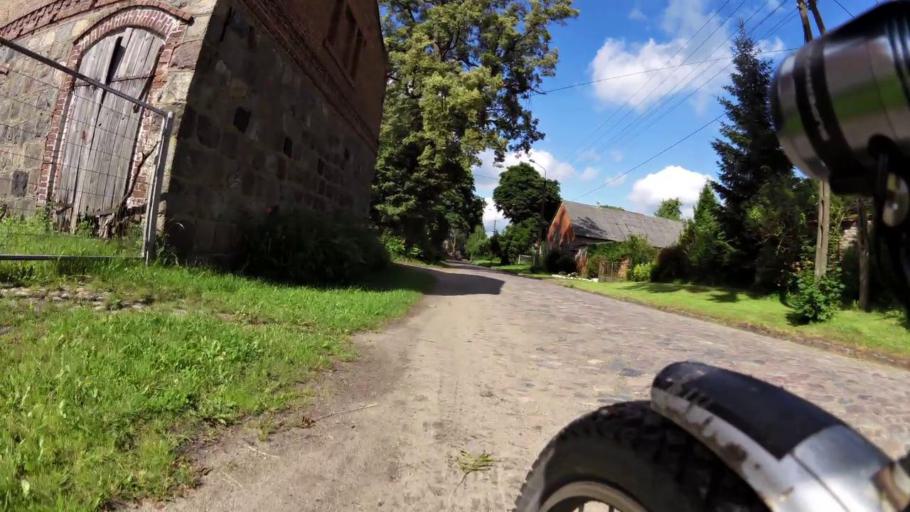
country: PL
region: West Pomeranian Voivodeship
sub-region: Powiat swidwinski
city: Swidwin
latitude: 53.7309
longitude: 15.7405
